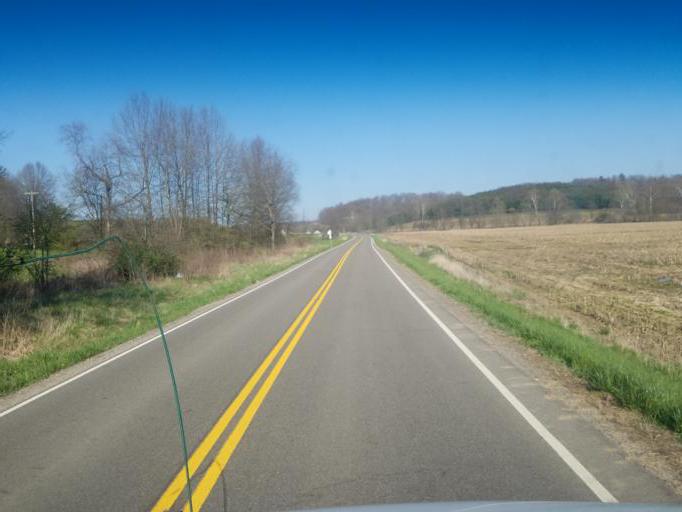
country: US
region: Ohio
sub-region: Muskingum County
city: Frazeysburg
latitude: 40.2432
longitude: -82.1367
